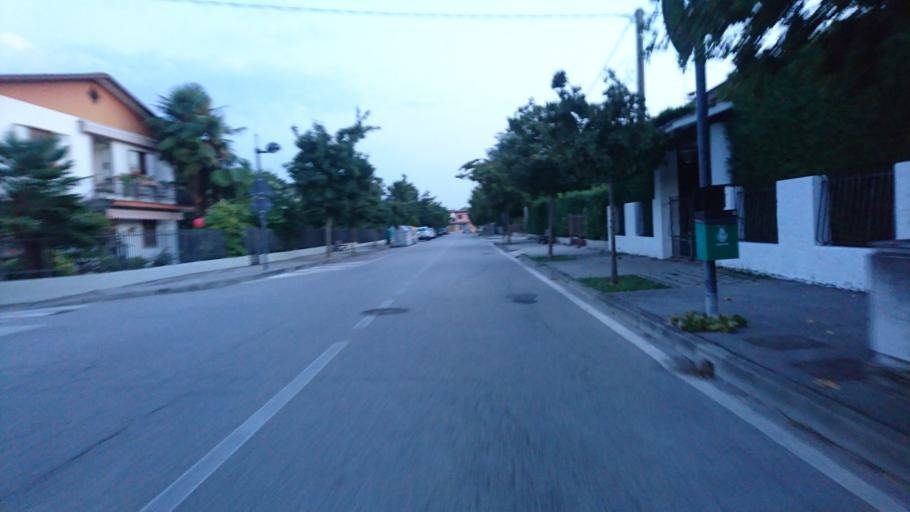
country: IT
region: Veneto
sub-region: Provincia di Padova
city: Abano Terme
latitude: 45.3644
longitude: 11.7929
